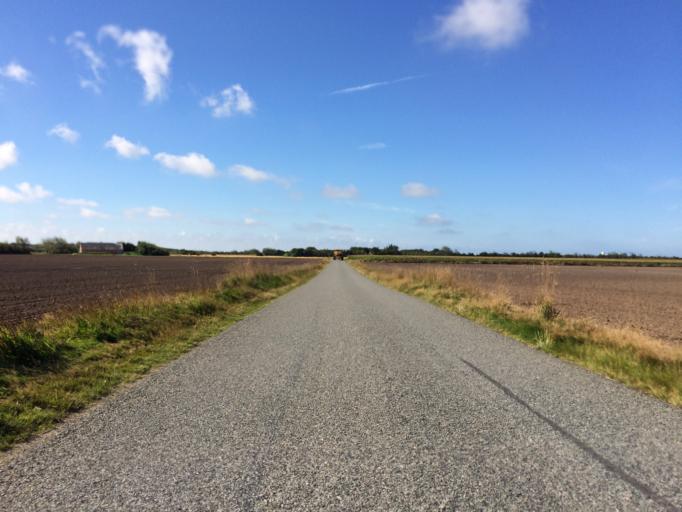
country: DK
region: Central Jutland
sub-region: Holstebro Kommune
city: Ulfborg
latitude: 56.2728
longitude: 8.1923
